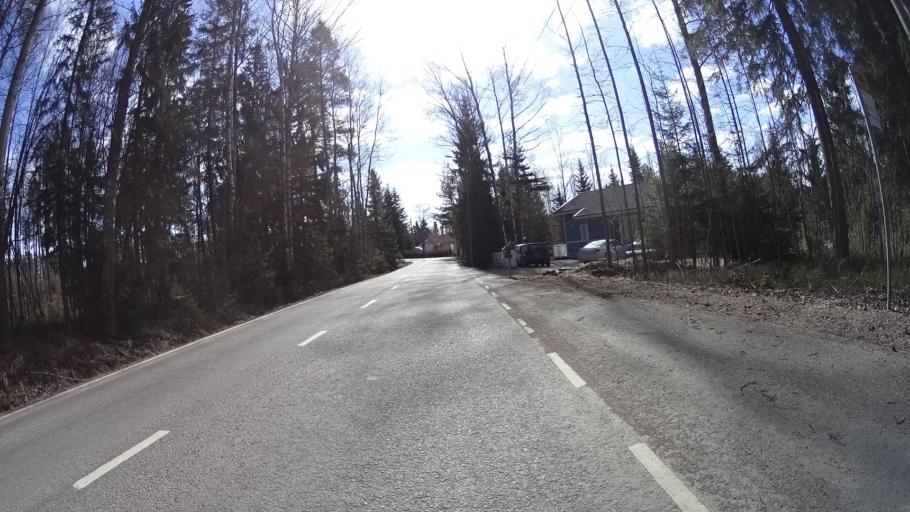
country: FI
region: Uusimaa
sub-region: Helsinki
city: Kauniainen
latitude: 60.2680
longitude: 24.7217
